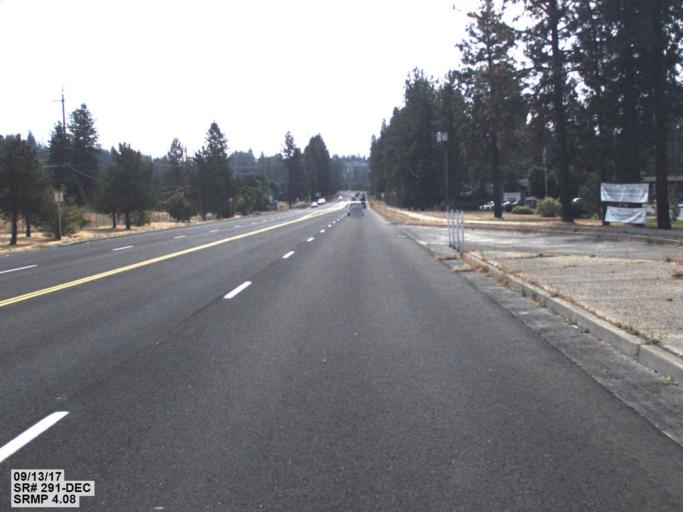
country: US
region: Washington
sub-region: Spokane County
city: Town and Country
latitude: 47.7243
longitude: -117.4933
